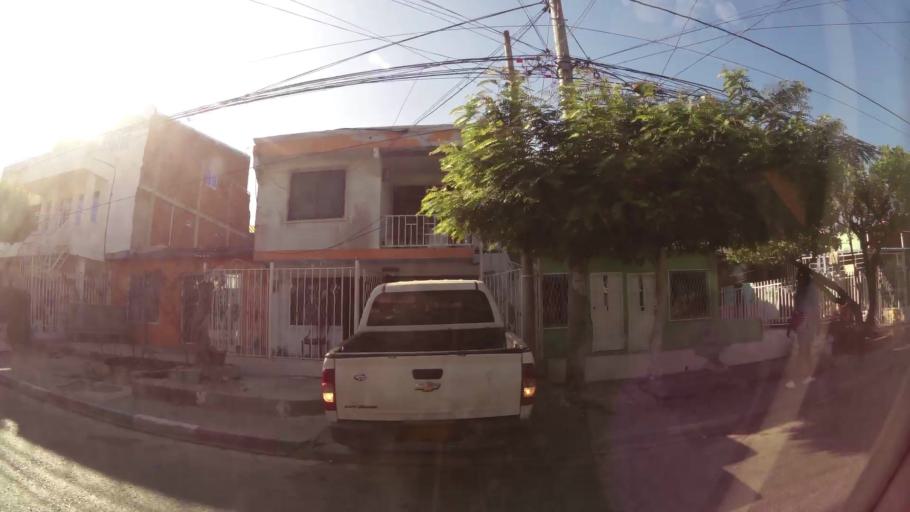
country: CO
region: Bolivar
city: Cartagena
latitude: 10.3915
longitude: -75.5023
